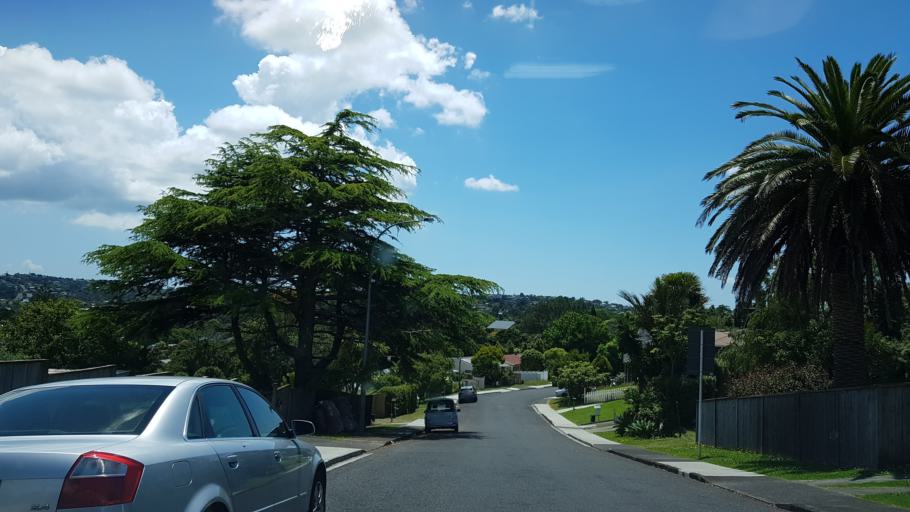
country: NZ
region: Auckland
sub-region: Auckland
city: North Shore
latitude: -36.7993
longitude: 174.7018
